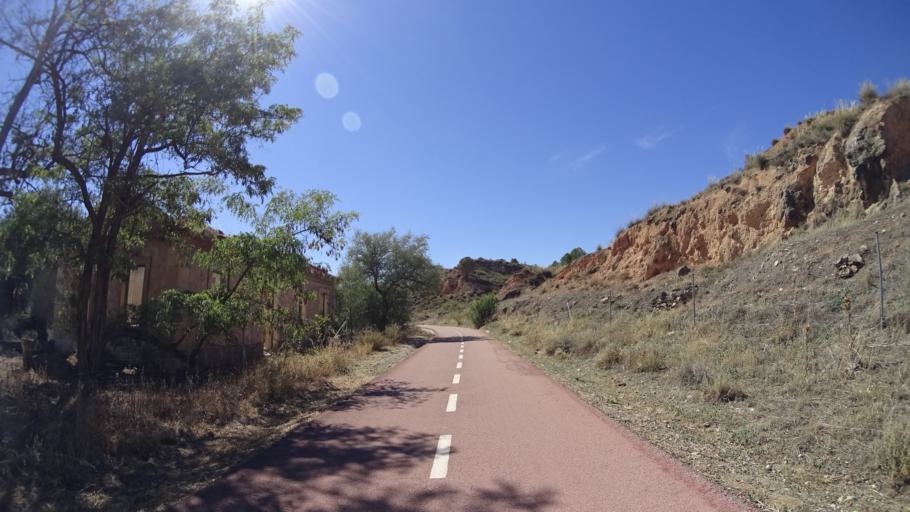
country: ES
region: Madrid
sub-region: Provincia de Madrid
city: Morata de Tajuna
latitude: 40.2312
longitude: -3.4629
